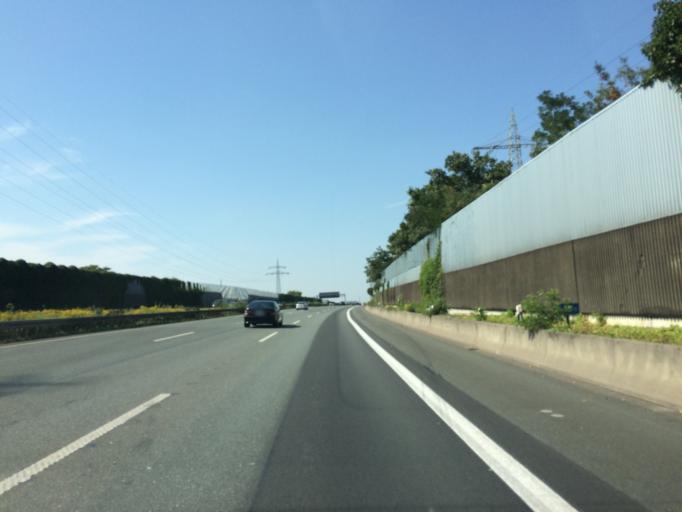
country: DE
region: North Rhine-Westphalia
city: Castrop-Rauxel
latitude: 51.5919
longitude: 7.3468
